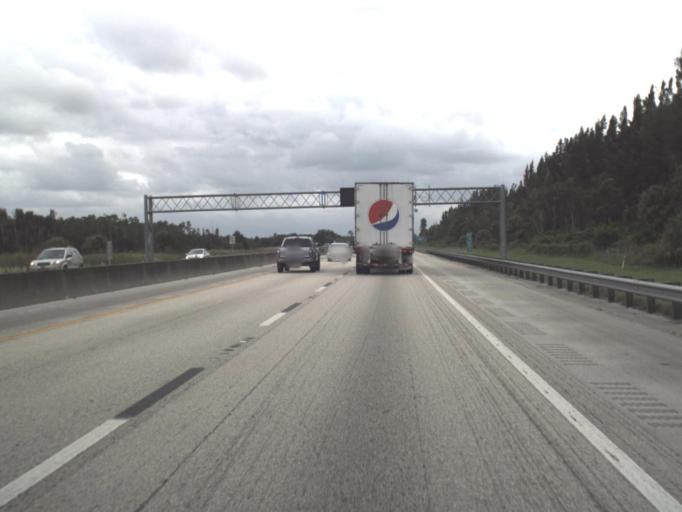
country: US
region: Florida
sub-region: Palm Beach County
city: Schall Circle
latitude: 26.7284
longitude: -80.1355
